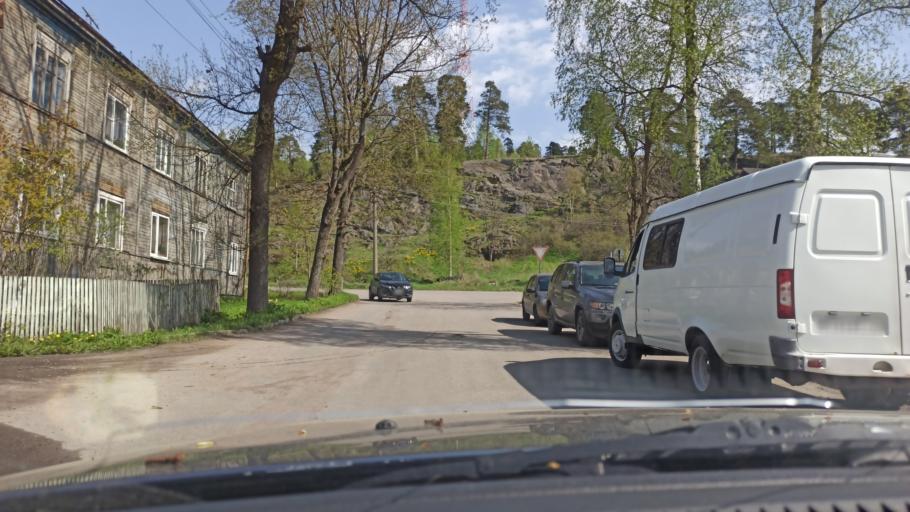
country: RU
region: Republic of Karelia
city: Lakhdenpokh'ya
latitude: 61.5207
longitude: 30.1987
